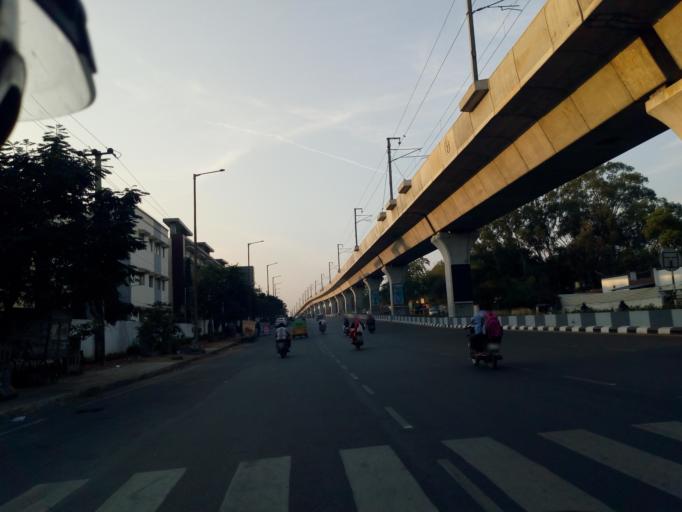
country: IN
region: Telangana
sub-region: Hyderabad
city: Malkajgiri
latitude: 17.4297
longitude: 78.5260
